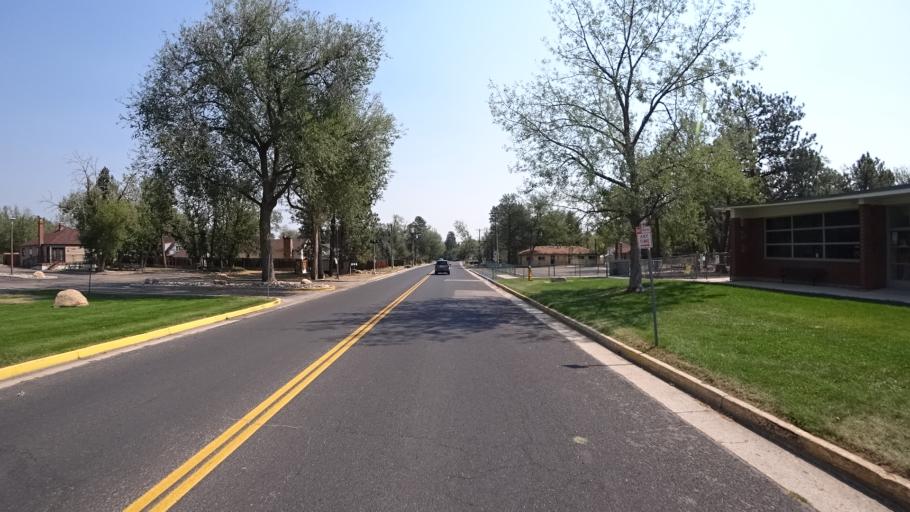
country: US
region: Colorado
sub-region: El Paso County
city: Colorado Springs
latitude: 38.7991
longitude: -104.8485
